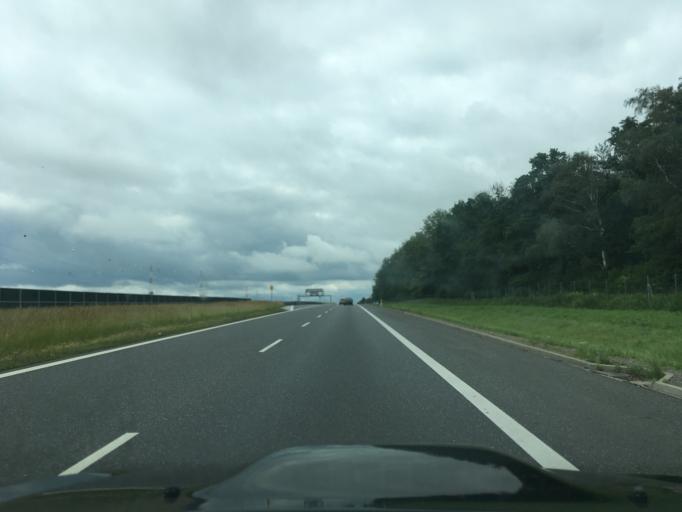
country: PL
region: Lublin Voivodeship
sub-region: Powiat swidnicki
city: Swidnik
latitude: 51.2198
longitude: 22.6561
